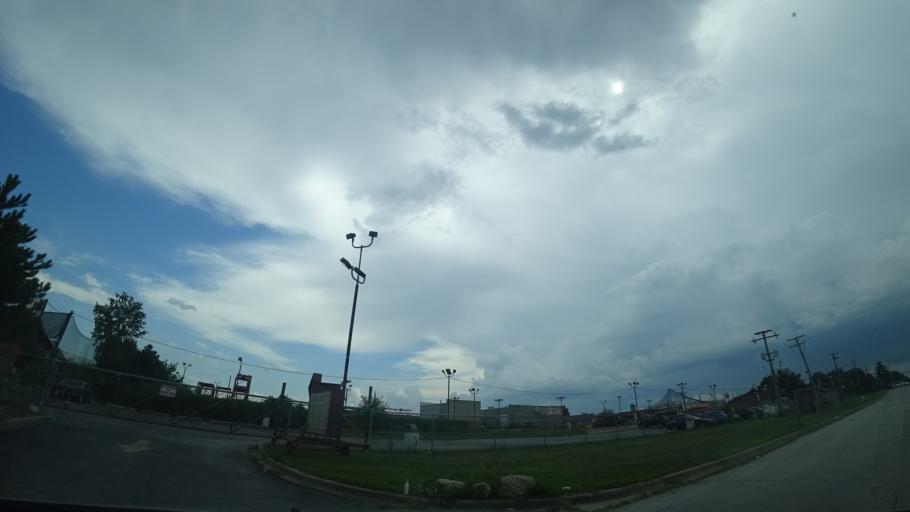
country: US
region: Illinois
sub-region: Cook County
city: Alsip
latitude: 41.6763
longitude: -87.7370
